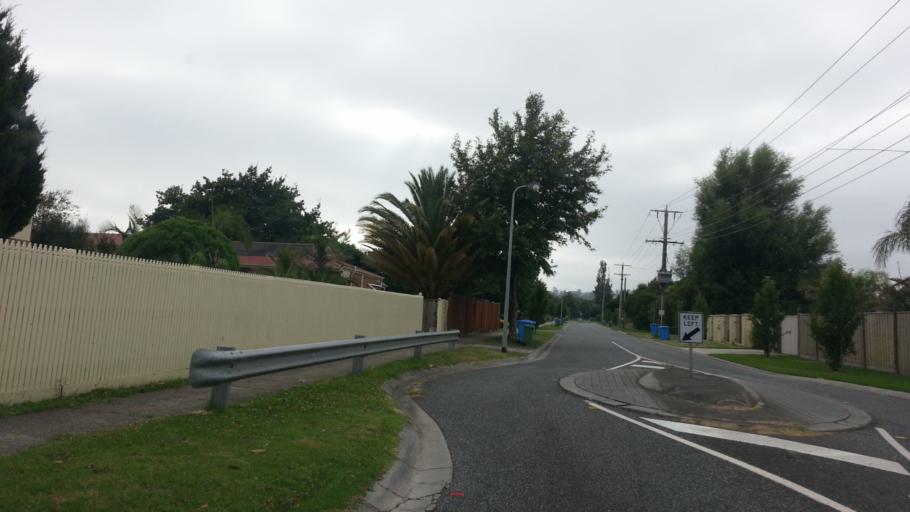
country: AU
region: Victoria
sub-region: Casey
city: Narre Warren North
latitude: -37.9890
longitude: 145.3182
